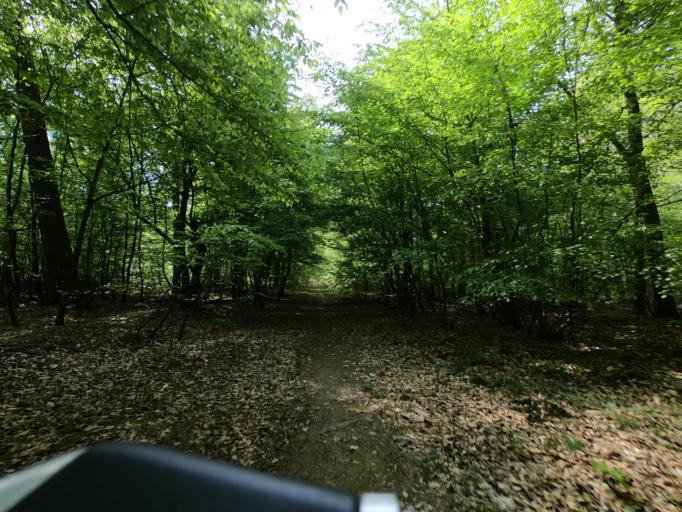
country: DE
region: Hesse
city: Morfelden-Walldorf
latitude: 50.0192
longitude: 8.5654
